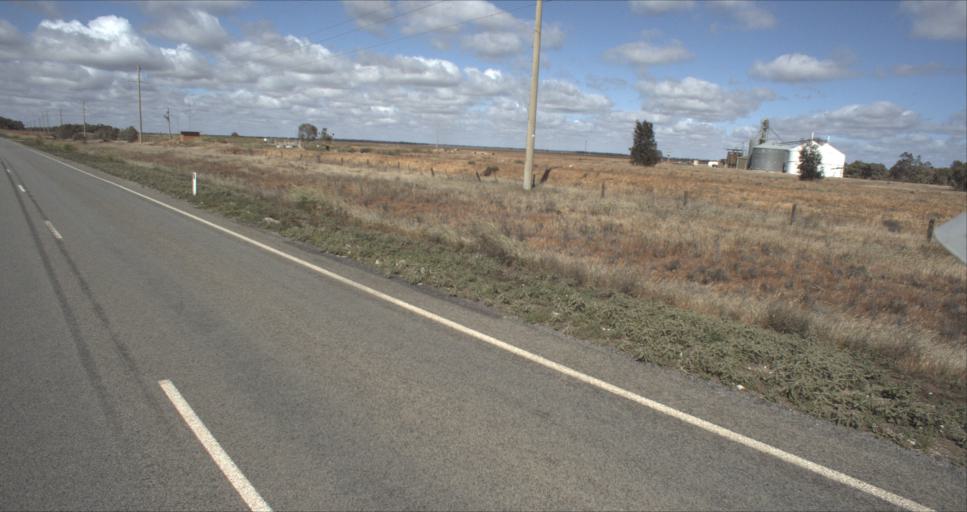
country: AU
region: New South Wales
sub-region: Murrumbidgee Shire
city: Darlington Point
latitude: -34.5473
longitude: 146.1711
